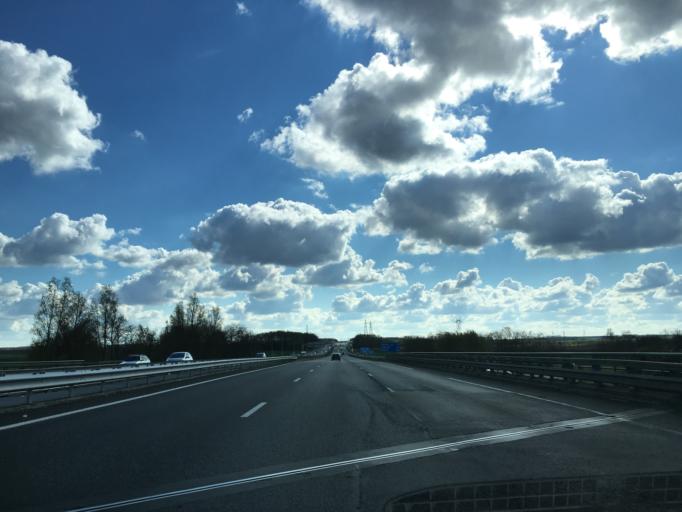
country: FR
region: Nord-Pas-de-Calais
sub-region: Departement du Pas-de-Calais
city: Biache-Saint-Vaast
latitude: 50.3342
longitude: 2.9218
